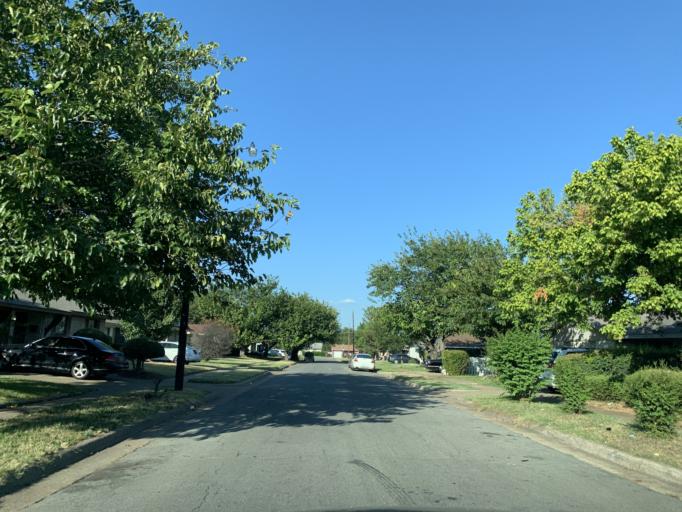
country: US
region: Texas
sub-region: Dallas County
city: Hutchins
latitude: 32.6636
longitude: -96.7627
